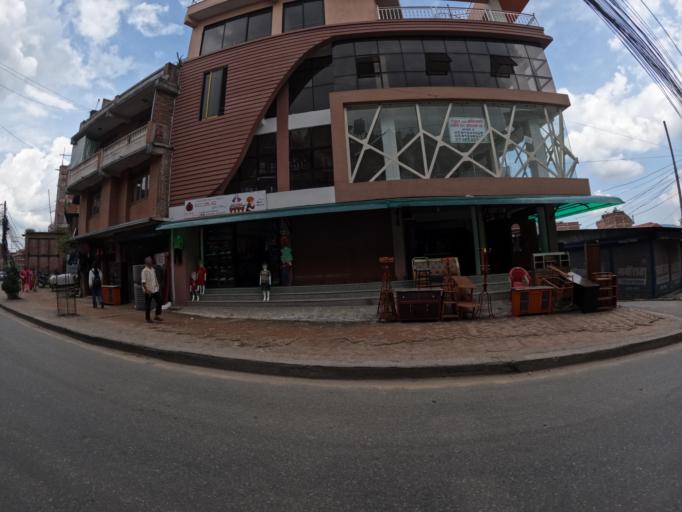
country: NP
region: Central Region
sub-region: Bagmati Zone
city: Bhaktapur
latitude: 27.6750
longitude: 85.4371
